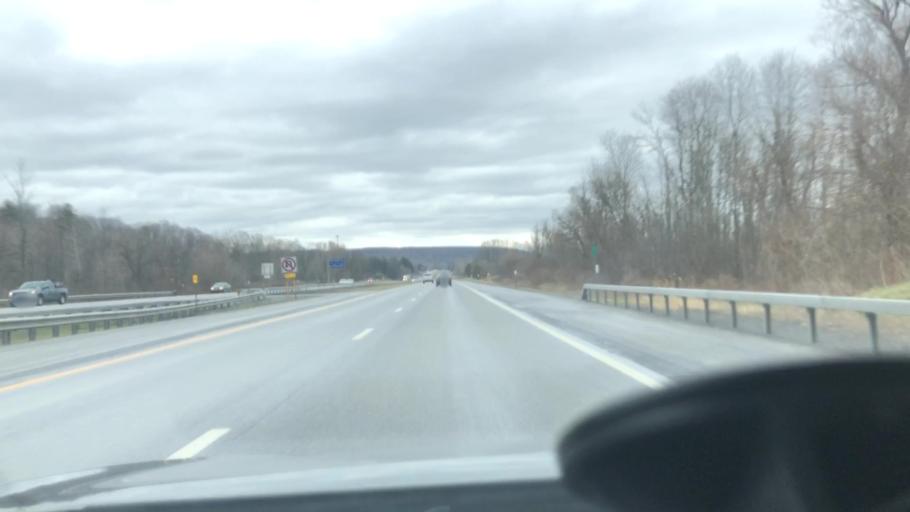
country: US
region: New York
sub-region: Herkimer County
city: Frankfort
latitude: 43.0721
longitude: -75.0975
